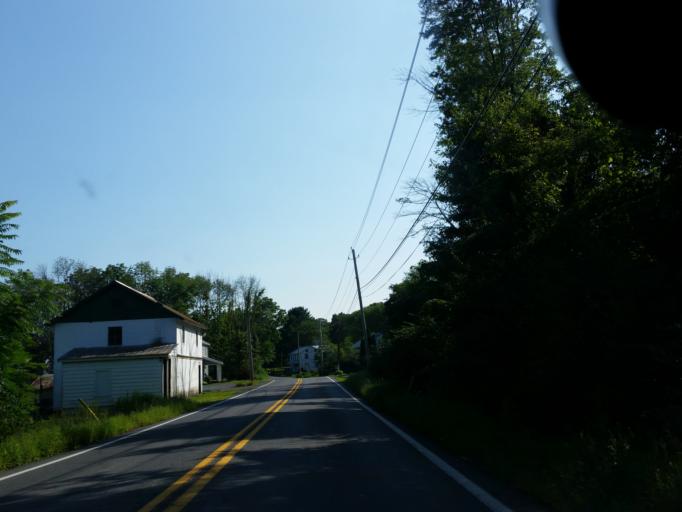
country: US
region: Pennsylvania
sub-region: Union County
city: Linntown
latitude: 41.0069
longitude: -76.9863
